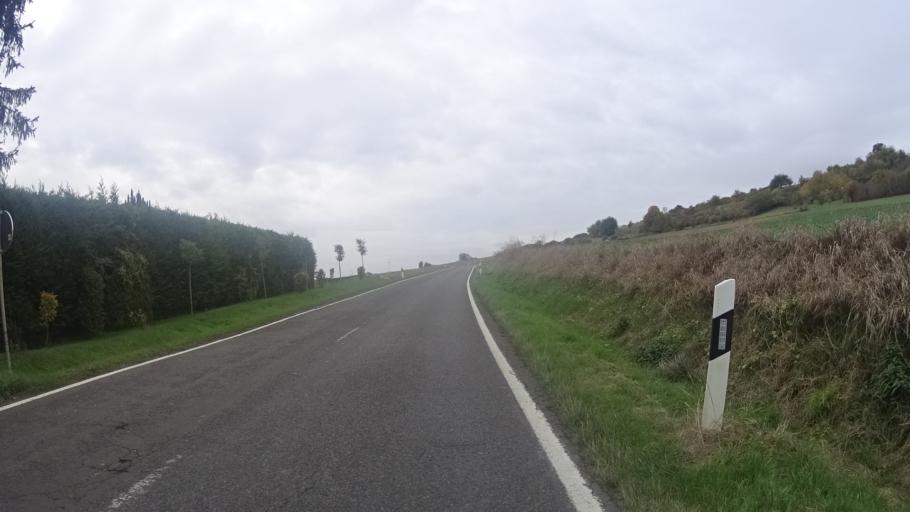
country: DE
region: Rheinland-Pfalz
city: Ottersheim
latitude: 49.6230
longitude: 8.1057
